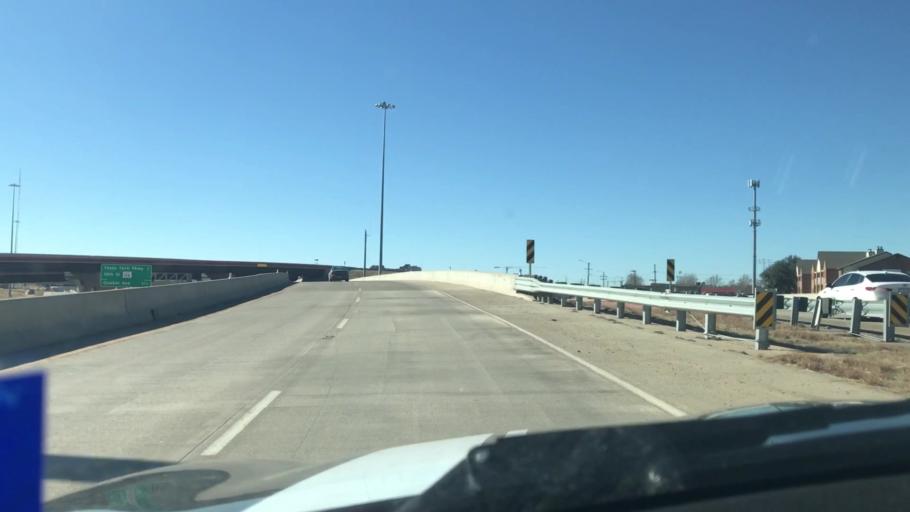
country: US
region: Texas
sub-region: Lubbock County
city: Lubbock
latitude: 33.5928
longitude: -101.8762
